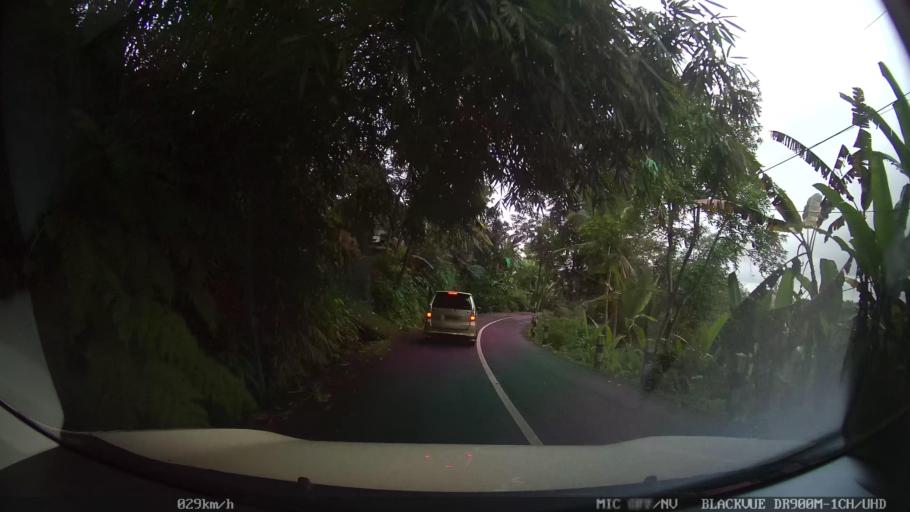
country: ID
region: Bali
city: Peneng
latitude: -8.3617
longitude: 115.1843
